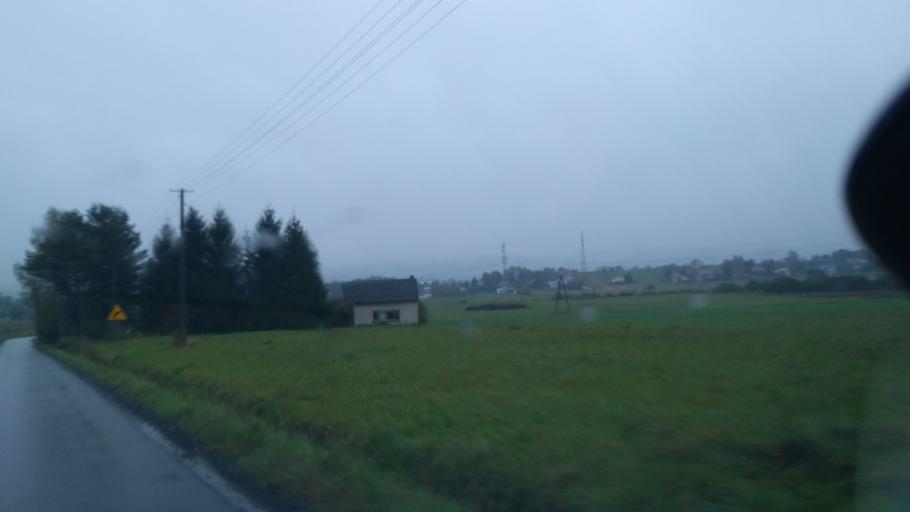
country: PL
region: Subcarpathian Voivodeship
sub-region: Powiat krosnienski
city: Korczyna
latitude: 49.6928
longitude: 21.8085
